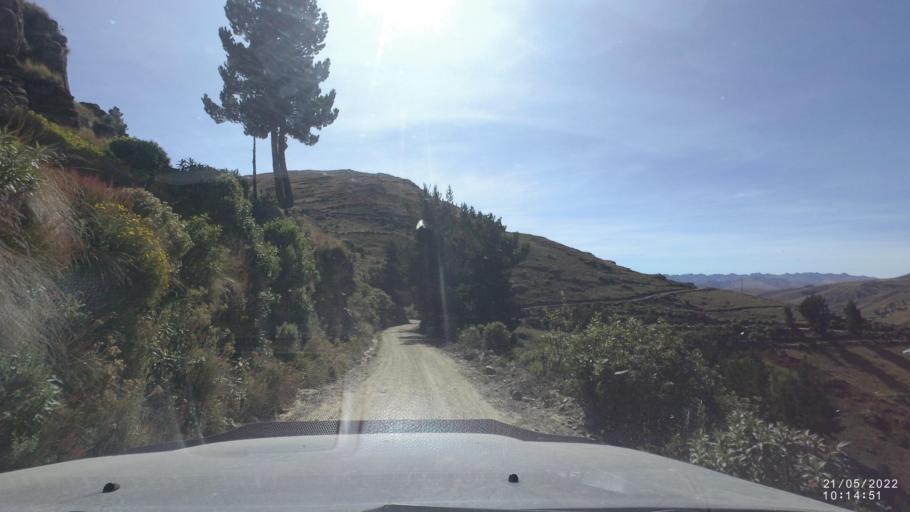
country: BO
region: Cochabamba
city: Colomi
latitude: -17.3322
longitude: -65.9697
